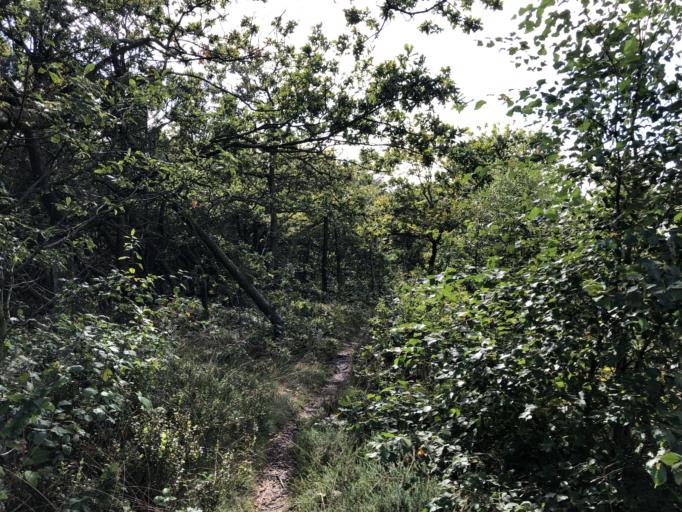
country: DK
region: Central Jutland
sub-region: Holstebro Kommune
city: Ulfborg
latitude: 56.3854
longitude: 8.3614
